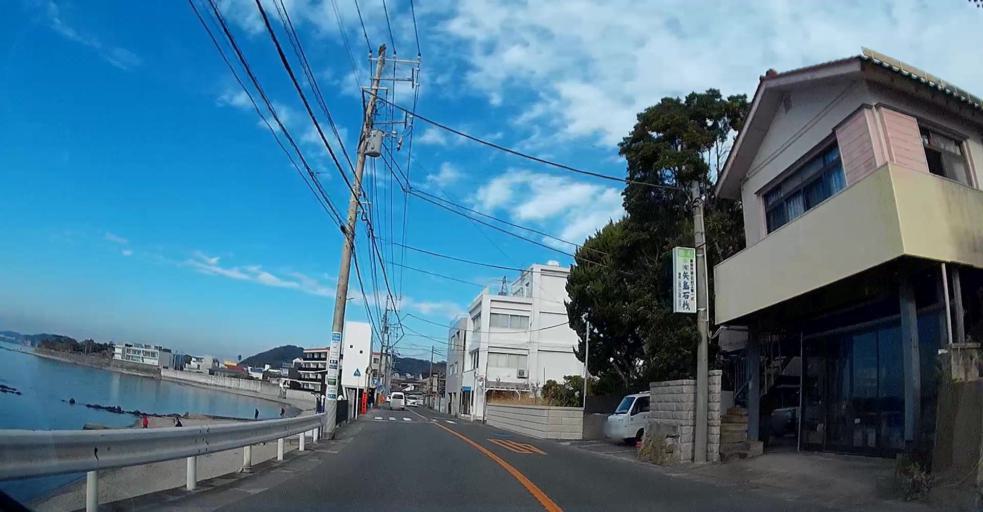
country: JP
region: Kanagawa
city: Hayama
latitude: 35.2693
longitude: 139.5709
